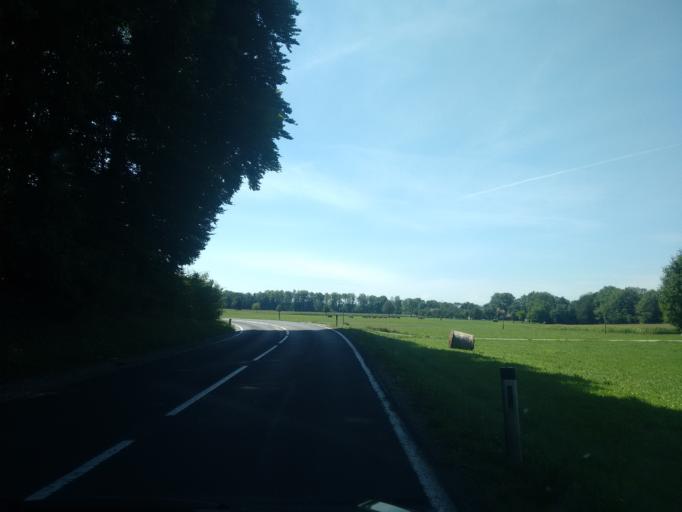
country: DE
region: Bavaria
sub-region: Lower Bavaria
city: Kirchdorf am Inn
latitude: 48.2183
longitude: 12.9871
